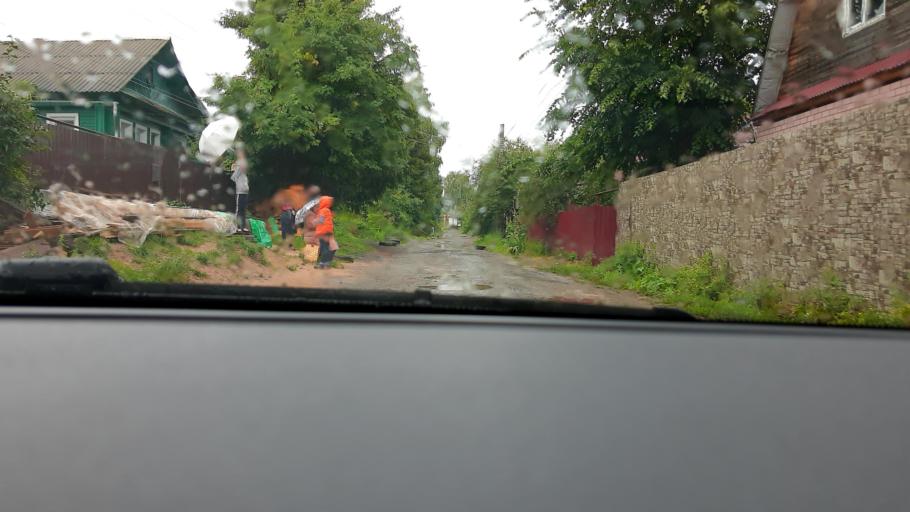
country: RU
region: Nizjnij Novgorod
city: Gorbatovka
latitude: 56.3697
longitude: 43.8342
